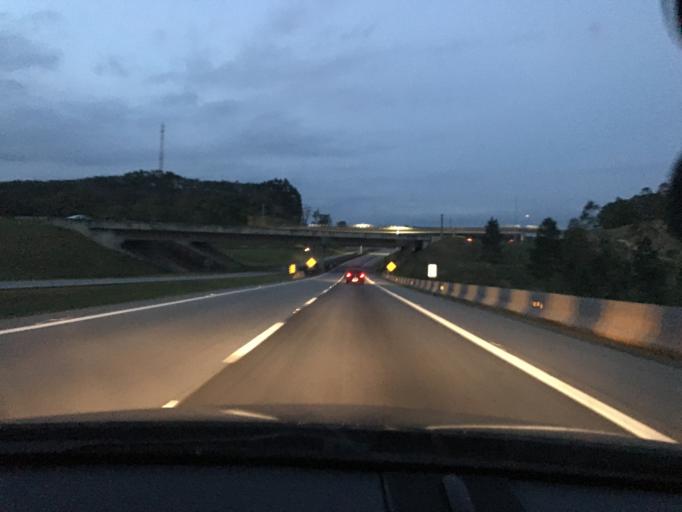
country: BR
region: Sao Paulo
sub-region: Santa Isabel
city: Santa Isabel
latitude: -23.3654
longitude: -46.1292
